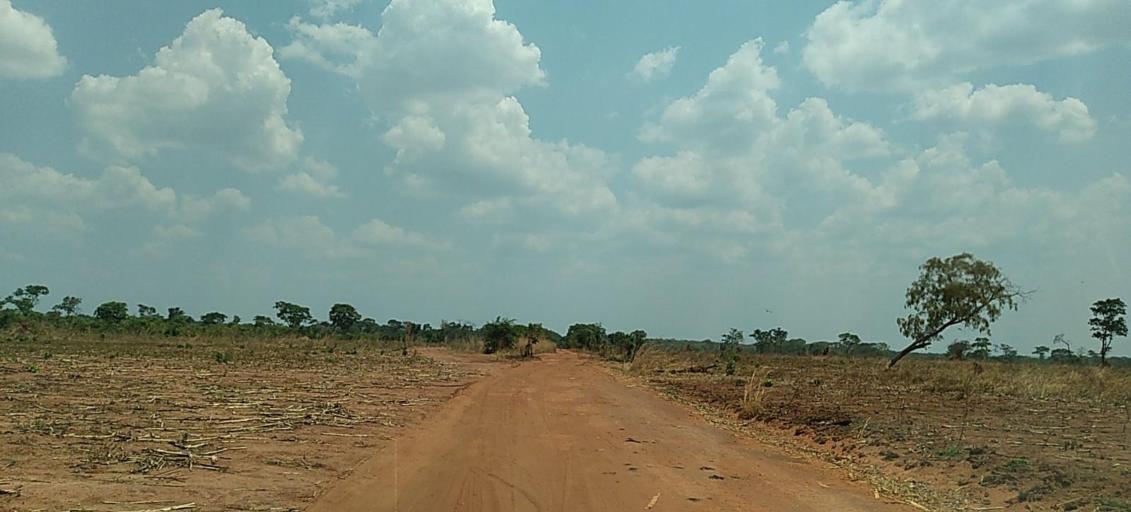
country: ZM
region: Copperbelt
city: Mpongwe
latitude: -13.6618
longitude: 28.0242
